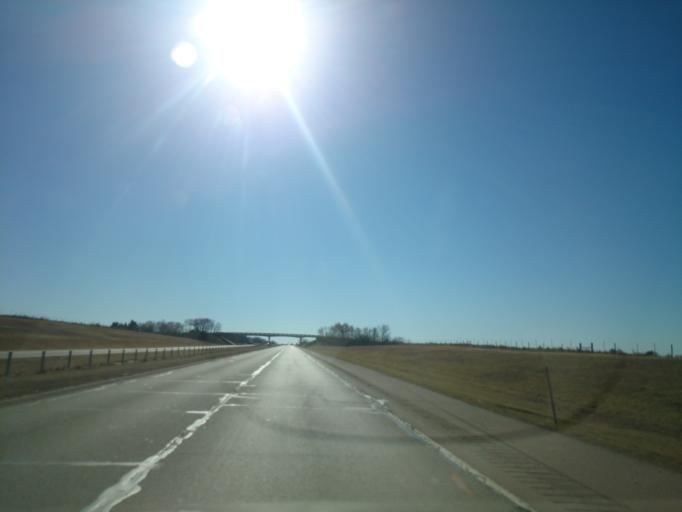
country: US
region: Oklahoma
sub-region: Logan County
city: Guthrie
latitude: 35.8666
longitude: -97.3944
